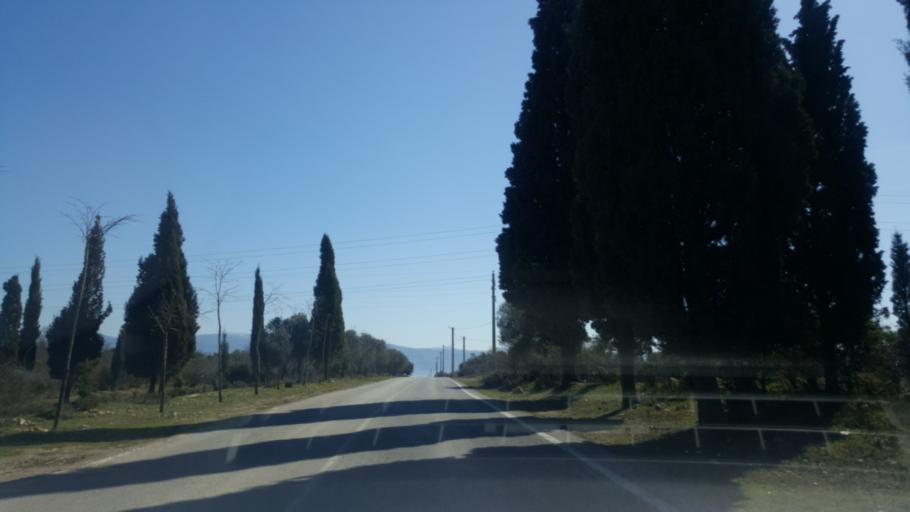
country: TR
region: Kocaeli
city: Tavsancil
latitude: 40.7839
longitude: 29.5737
